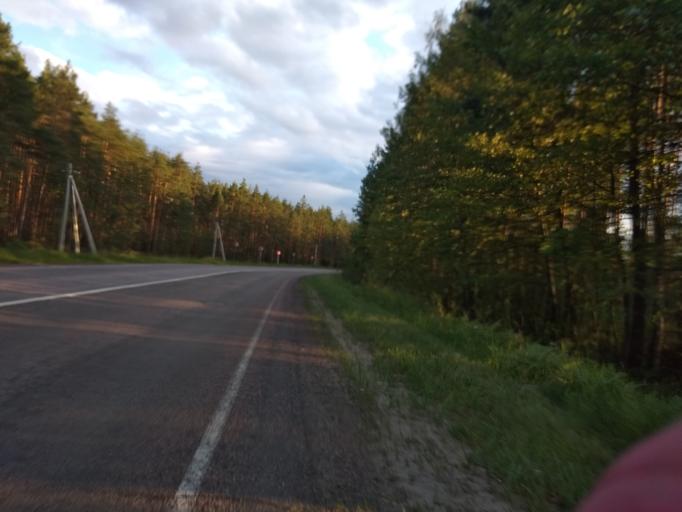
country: RU
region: Moskovskaya
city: Misheronskiy
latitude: 55.6279
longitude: 39.7399
